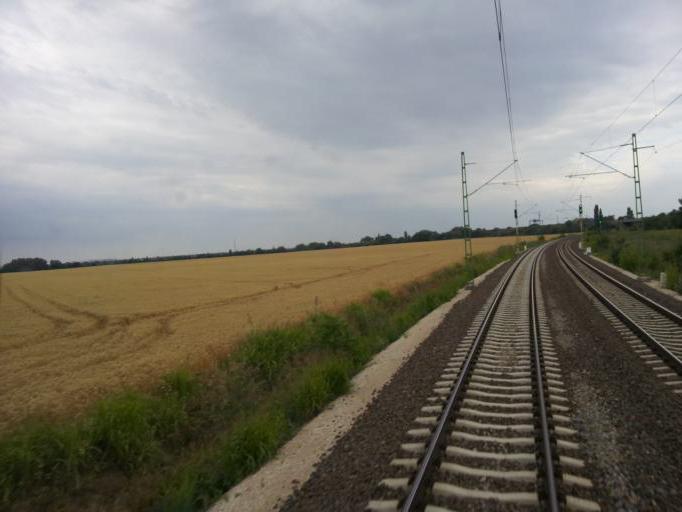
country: HU
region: Fejer
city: Szekesfehervar
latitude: 47.1700
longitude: 18.4741
